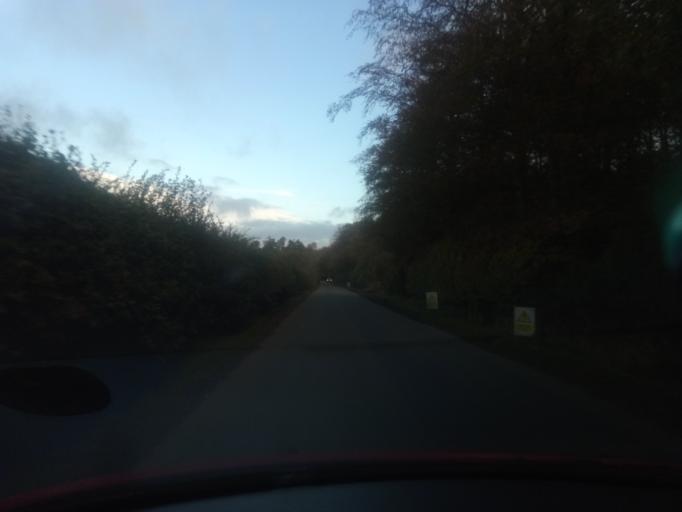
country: GB
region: Scotland
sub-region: The Scottish Borders
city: Jedburgh
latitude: 55.3854
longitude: -2.6429
